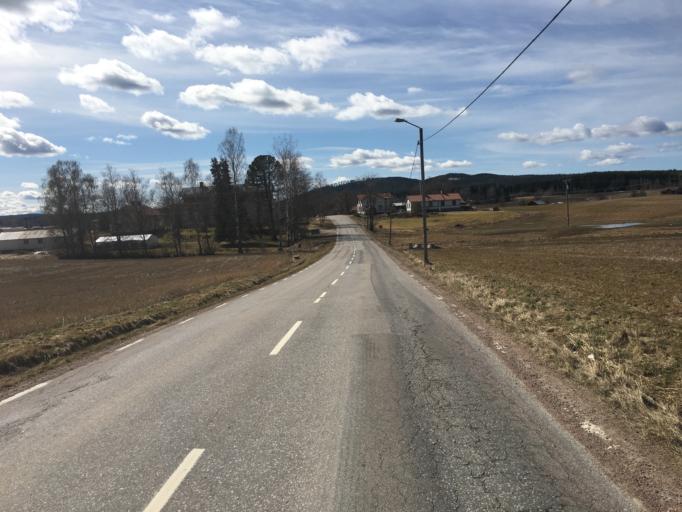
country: SE
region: Gaevleborg
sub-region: Hofors Kommun
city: Hofors
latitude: 60.5088
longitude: 16.4613
